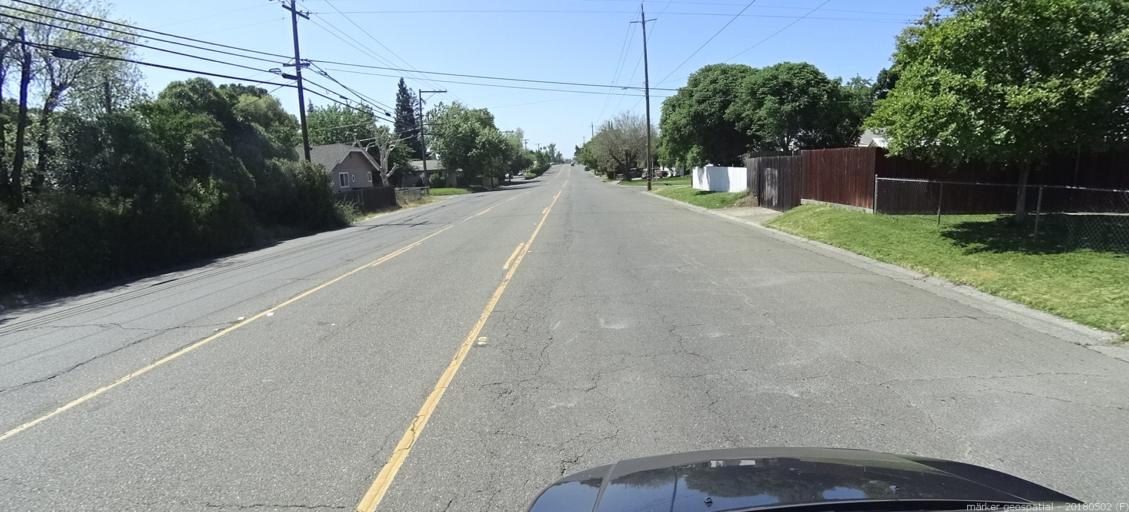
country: US
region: California
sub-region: Sacramento County
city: Arden-Arcade
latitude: 38.6068
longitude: -121.4200
